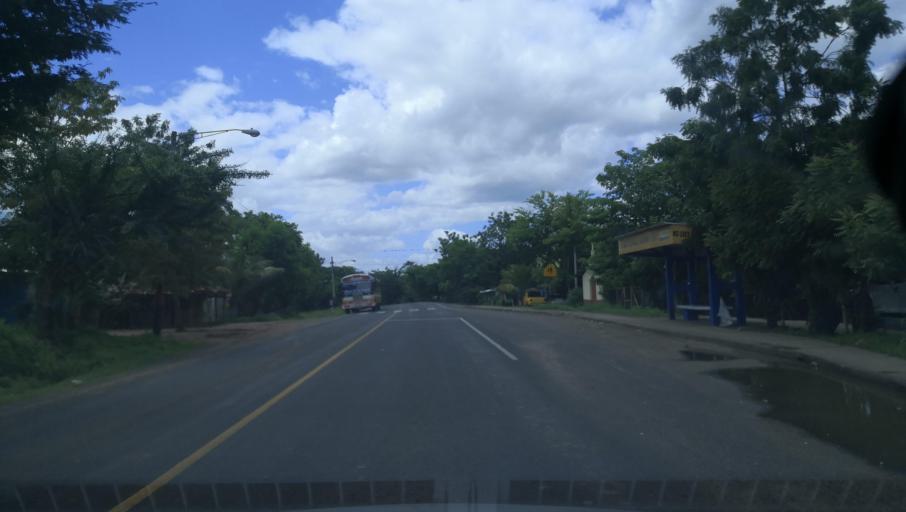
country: NI
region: Madriz
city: Palacaguina
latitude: 13.4113
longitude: -86.3994
